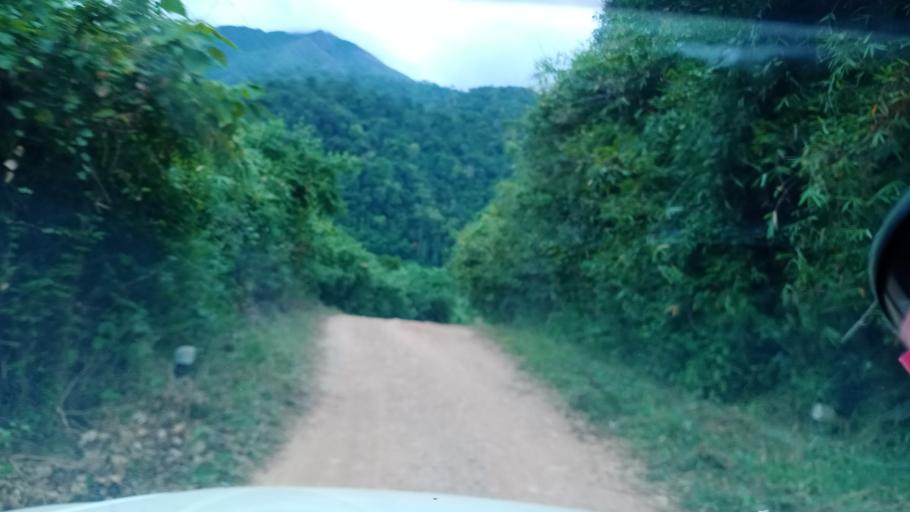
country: TH
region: Changwat Bueng Kan
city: Pak Khat
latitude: 18.7238
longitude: 103.2534
